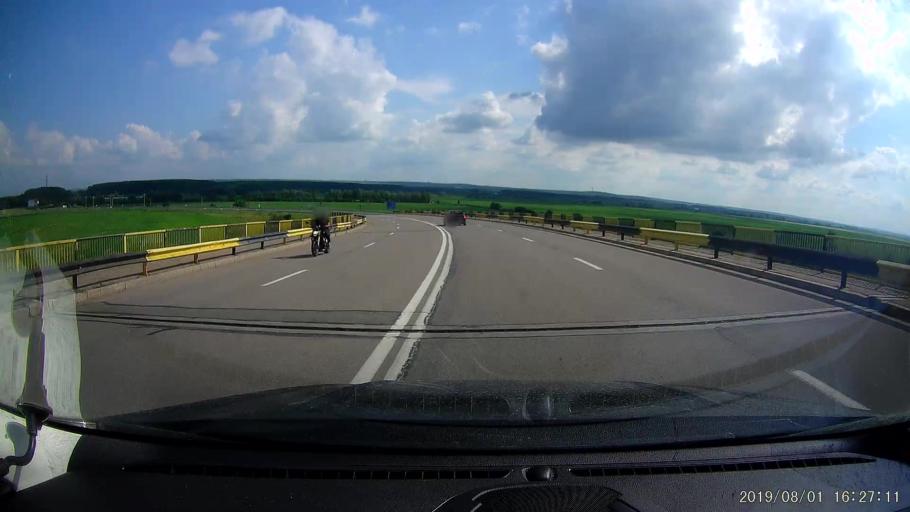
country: RO
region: Calarasi
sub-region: Municipiul Calarasi
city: Calarasi
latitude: 44.1667
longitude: 27.3109
